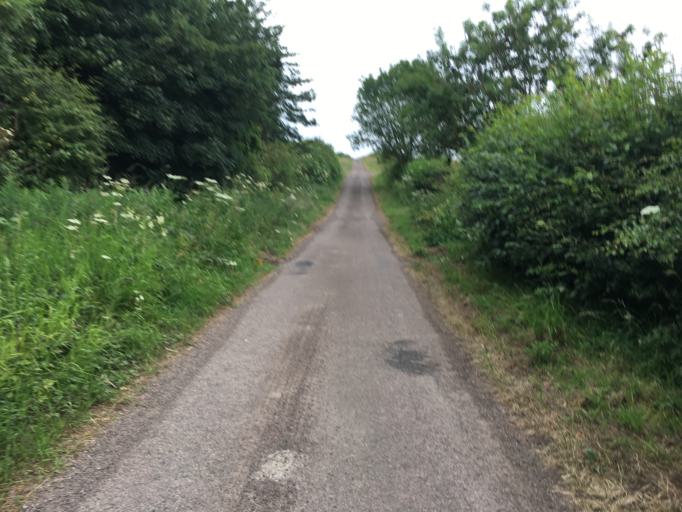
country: GB
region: England
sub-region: Northumberland
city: Lowick
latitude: 55.6605
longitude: -1.9082
